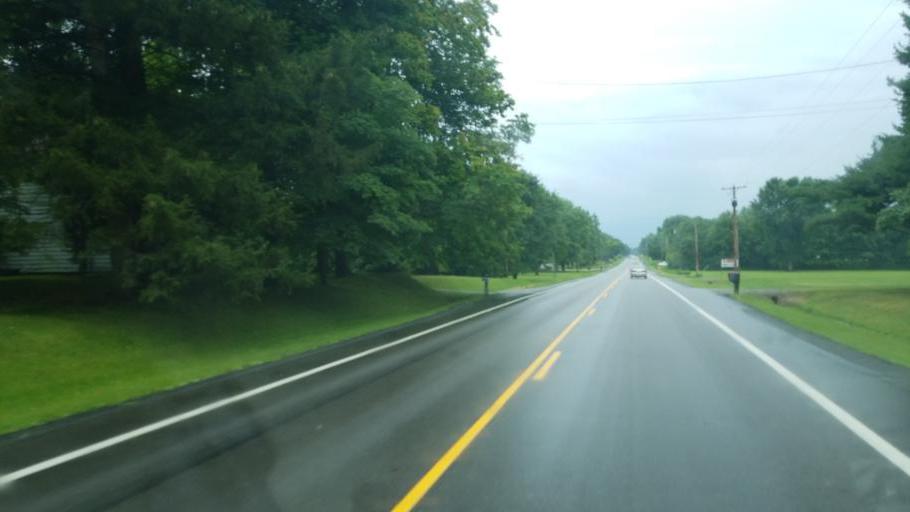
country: US
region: Ohio
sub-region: Trumbull County
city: Champion Heights
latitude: 41.4034
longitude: -80.8691
